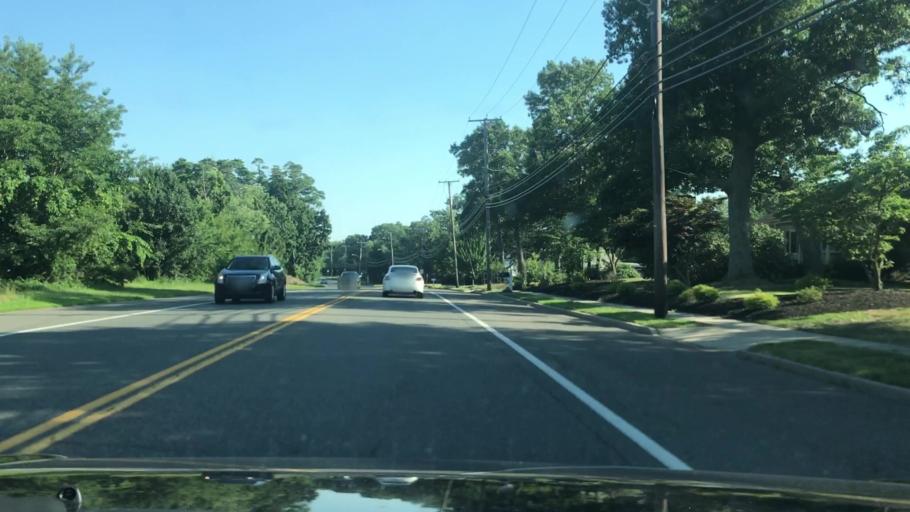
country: US
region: New Jersey
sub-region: Ocean County
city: Leisure Village
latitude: 40.0087
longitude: -74.2025
